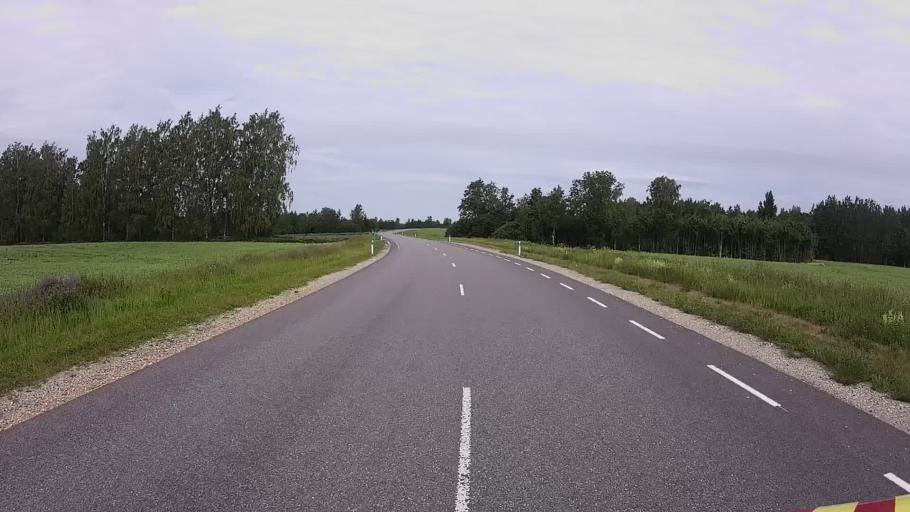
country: EE
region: Viljandimaa
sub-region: Karksi vald
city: Karksi-Nuia
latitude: 58.1585
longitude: 25.5928
